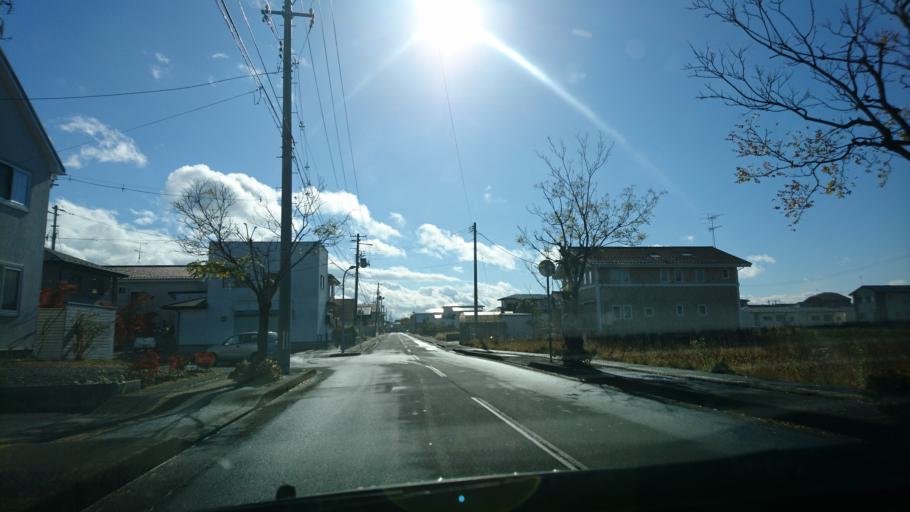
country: JP
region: Iwate
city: Ichinoseki
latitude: 38.9431
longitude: 141.1314
